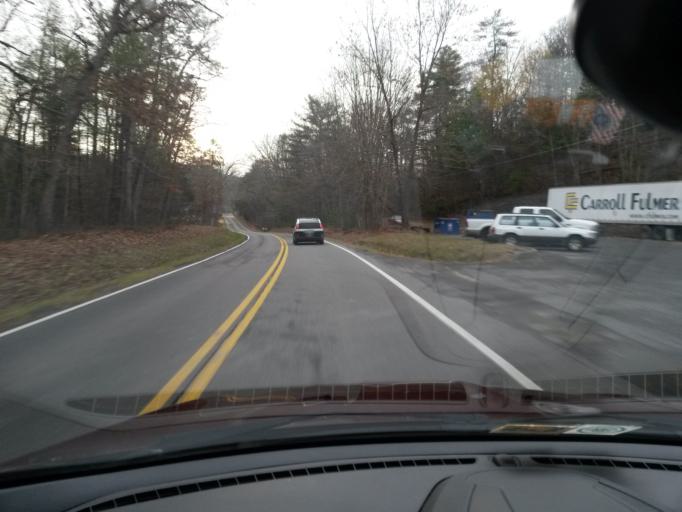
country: US
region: Virginia
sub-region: Alleghany County
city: Clifton Forge
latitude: 37.8202
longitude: -79.7493
